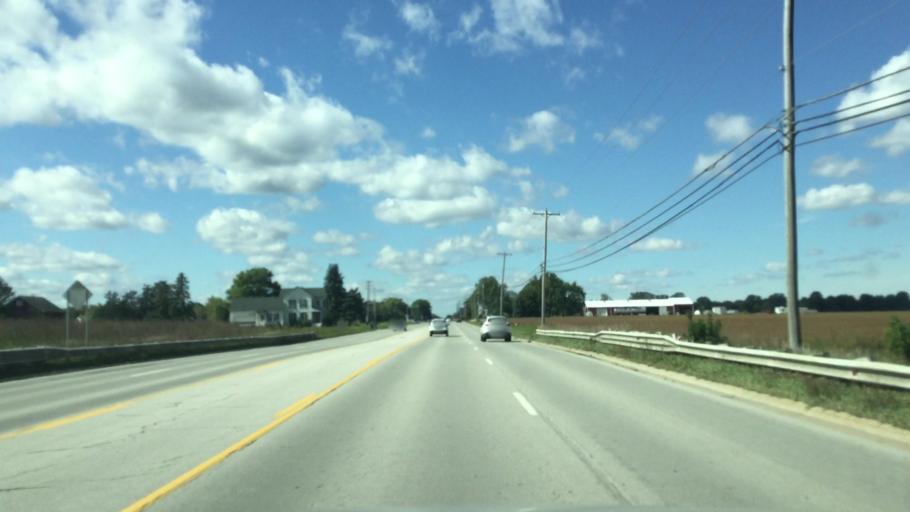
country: US
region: Michigan
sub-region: Genesee County
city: Swartz Creek
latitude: 42.9437
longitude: -83.7536
